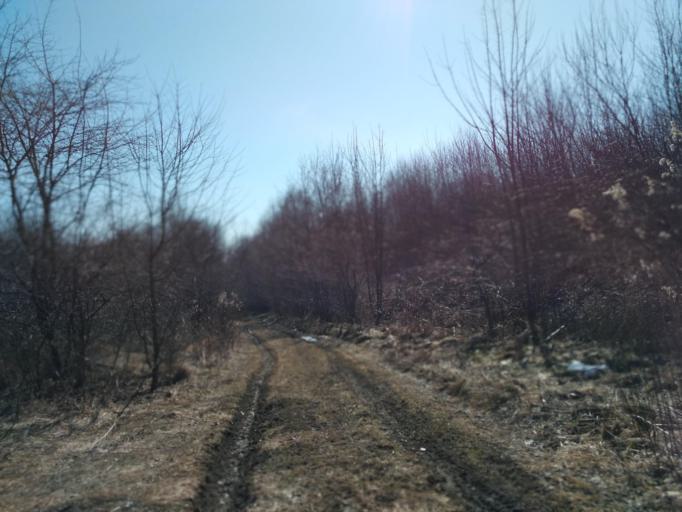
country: PL
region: Subcarpathian Voivodeship
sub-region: Powiat brzozowski
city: Domaradz
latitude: 49.8017
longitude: 21.9622
